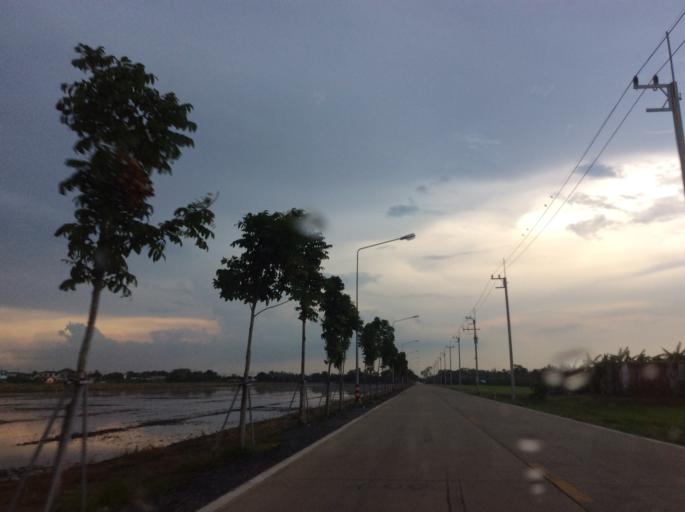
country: TH
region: Pathum Thani
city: Thanyaburi
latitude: 14.0029
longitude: 100.7365
